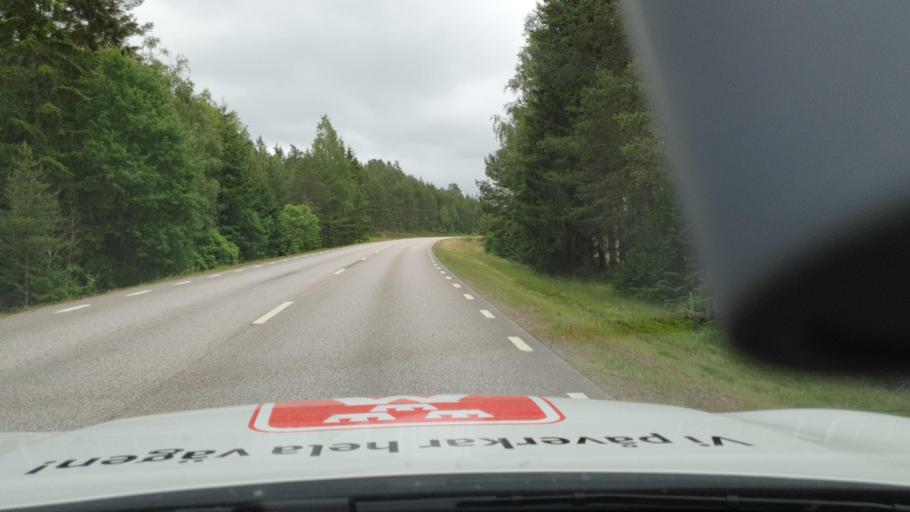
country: SE
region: Vaestra Goetaland
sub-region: Tibro Kommun
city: Tibro
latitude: 58.3632
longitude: 14.2126
